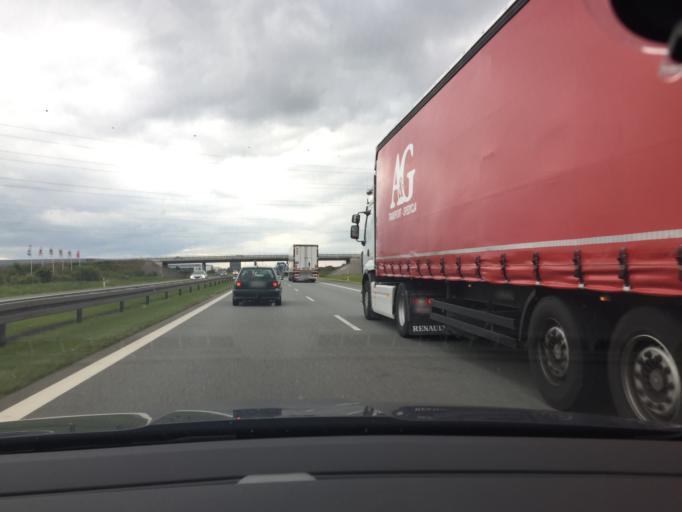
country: PL
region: Greater Poland Voivodeship
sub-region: Powiat poznanski
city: Komorniki
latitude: 52.3505
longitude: 16.8080
